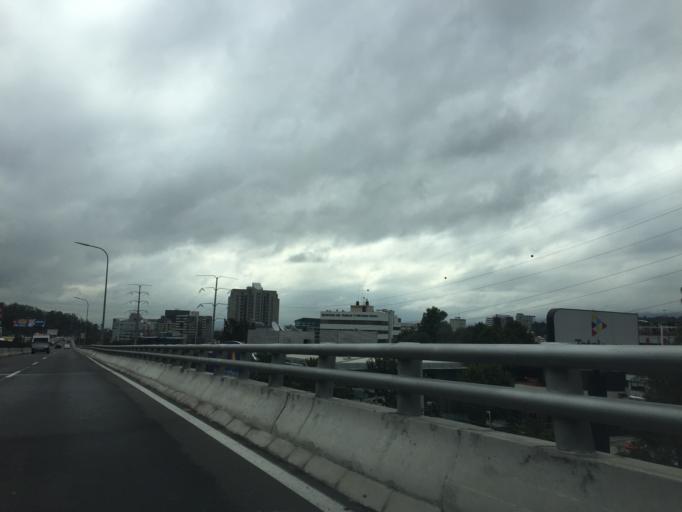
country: MX
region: Mexico City
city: Magdalena Contreras
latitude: 19.3065
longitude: -99.2105
